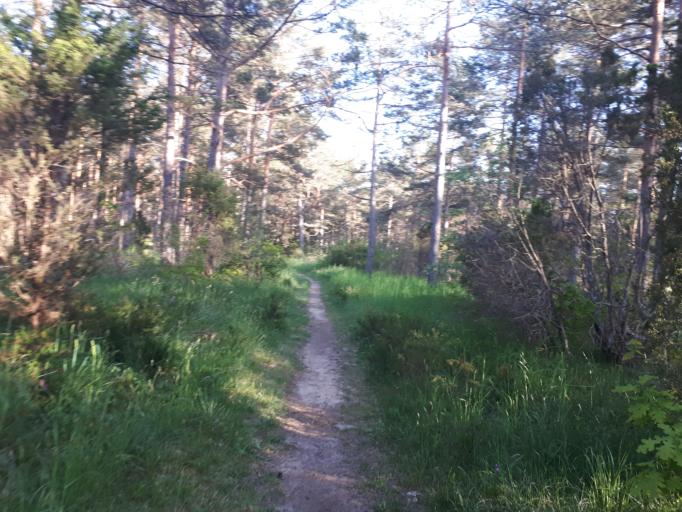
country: SE
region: Gotland
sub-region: Gotland
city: Visby
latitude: 57.6047
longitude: 18.2980
